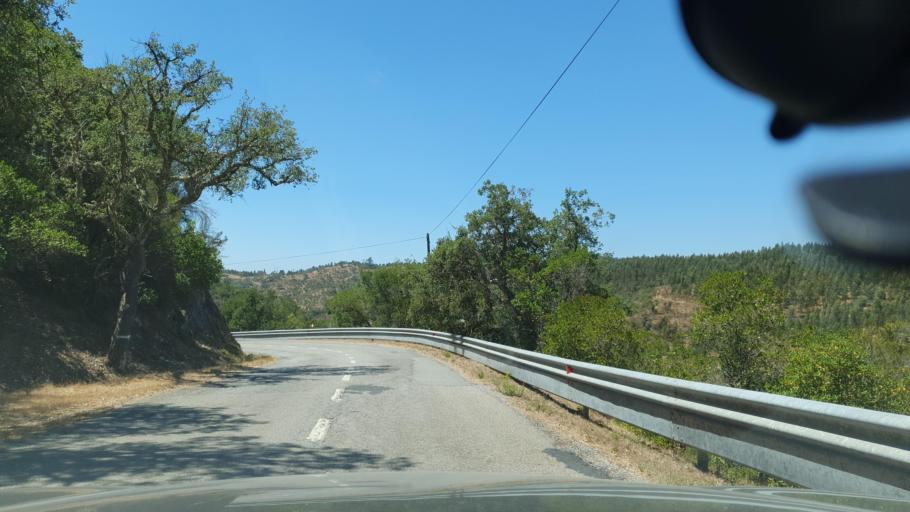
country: PT
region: Beja
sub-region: Odemira
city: Odemira
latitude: 37.6025
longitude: -8.5707
